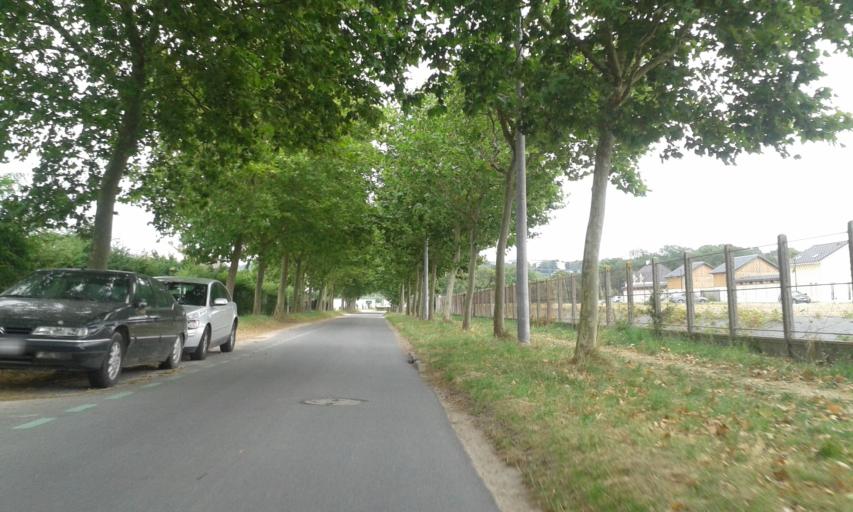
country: FR
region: Ile-de-France
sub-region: Departement du Val-d'Oise
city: La Frette-sur-Seine
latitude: 48.9623
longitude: 2.1719
